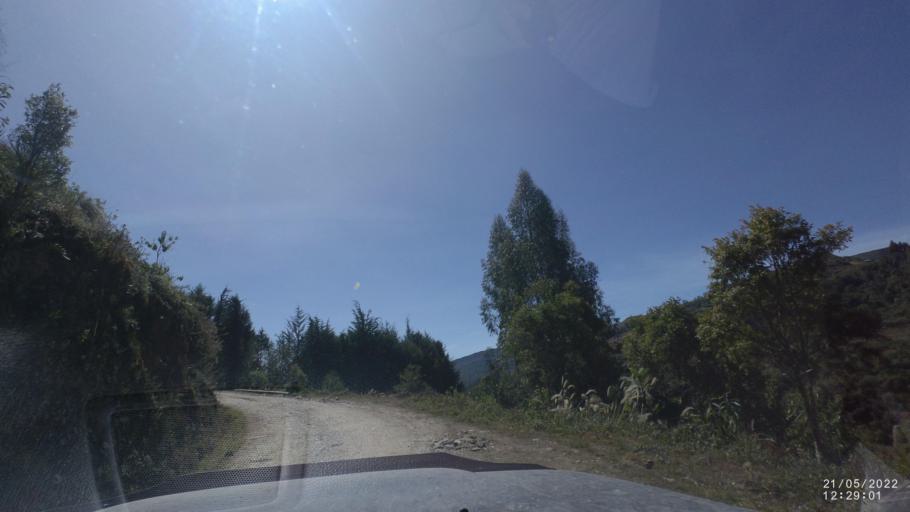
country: BO
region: Cochabamba
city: Colomi
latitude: -17.2177
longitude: -65.9119
